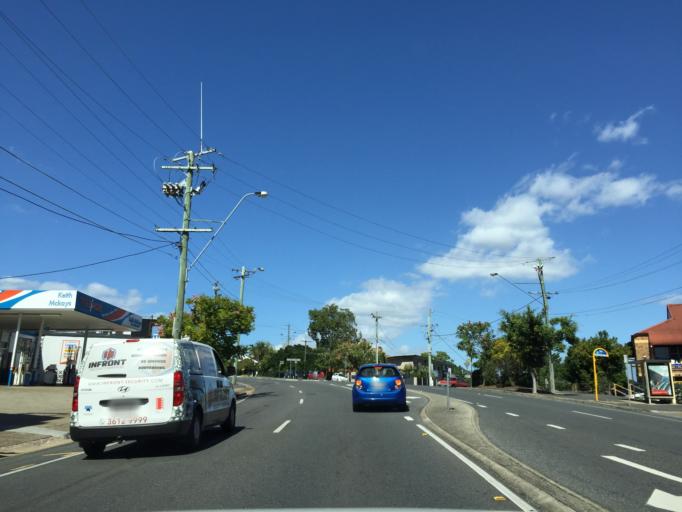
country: AU
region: Queensland
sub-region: Brisbane
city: Milton
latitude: -27.4549
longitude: 153.0069
